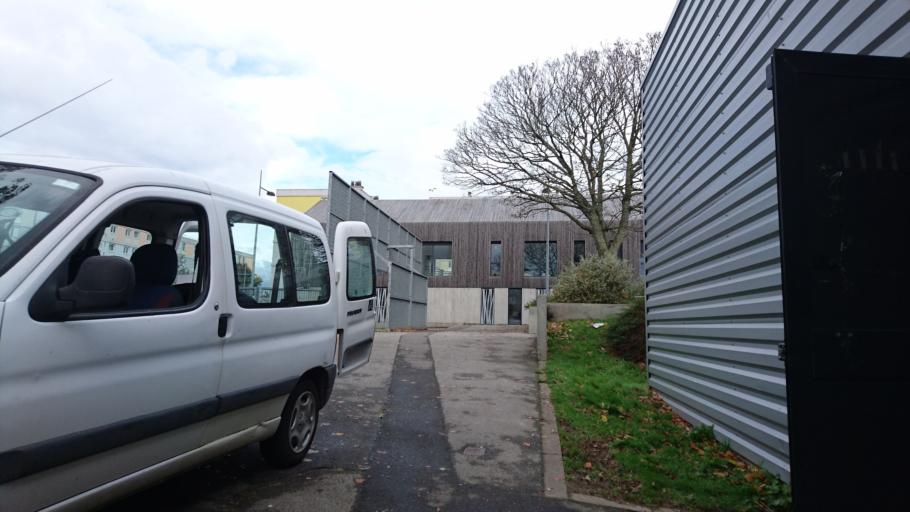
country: FR
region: Brittany
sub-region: Departement du Finistere
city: Brest
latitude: 48.4129
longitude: -4.4730
